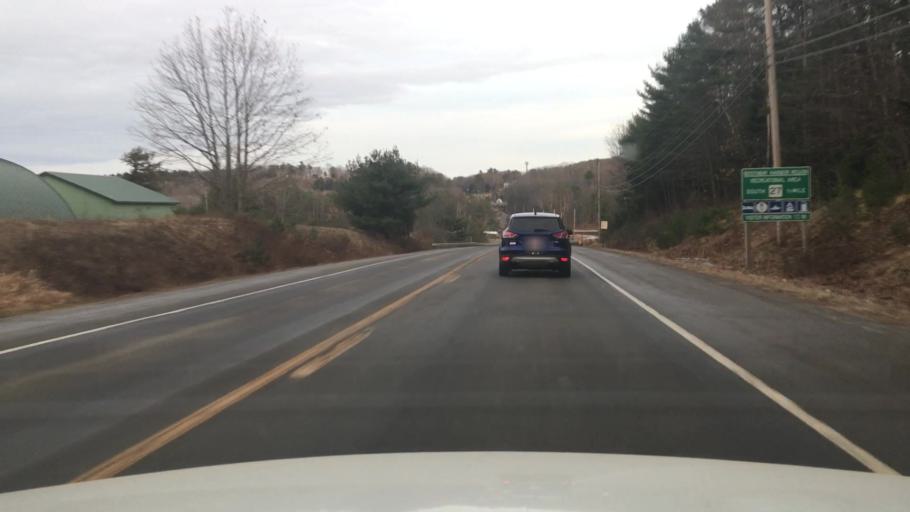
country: US
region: Maine
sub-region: Lincoln County
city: Wiscasset
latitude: 43.9999
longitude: -69.6469
